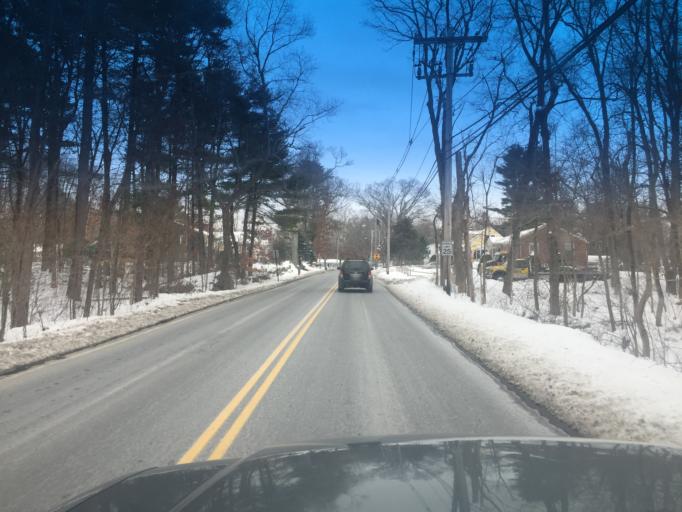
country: US
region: Massachusetts
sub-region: Norfolk County
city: Norfolk
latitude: 42.1131
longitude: -71.2860
